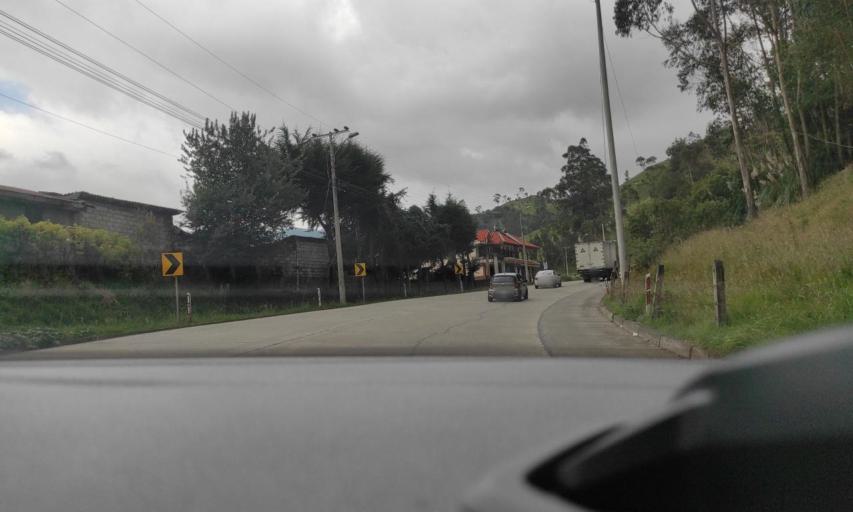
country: EC
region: Canar
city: Azogues
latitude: -2.6742
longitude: -78.8954
